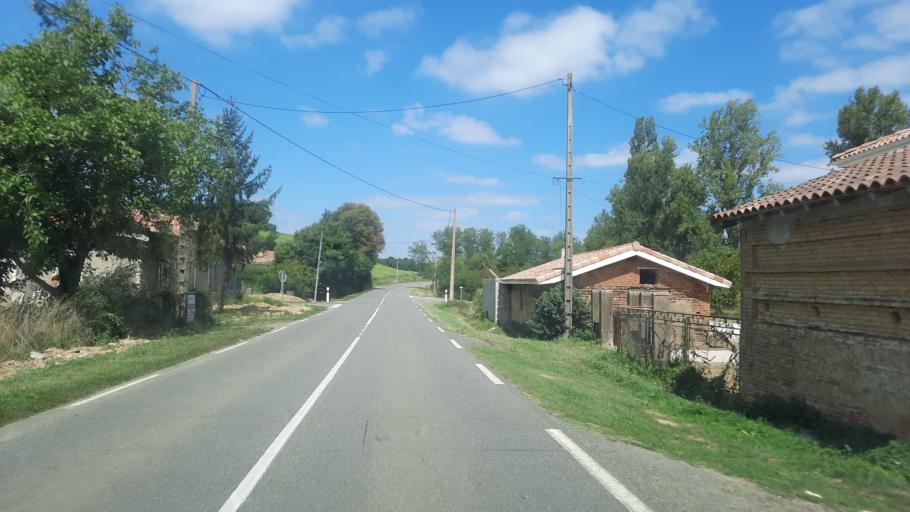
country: FR
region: Midi-Pyrenees
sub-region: Departement du Gers
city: Lombez
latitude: 43.4384
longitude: 0.8501
